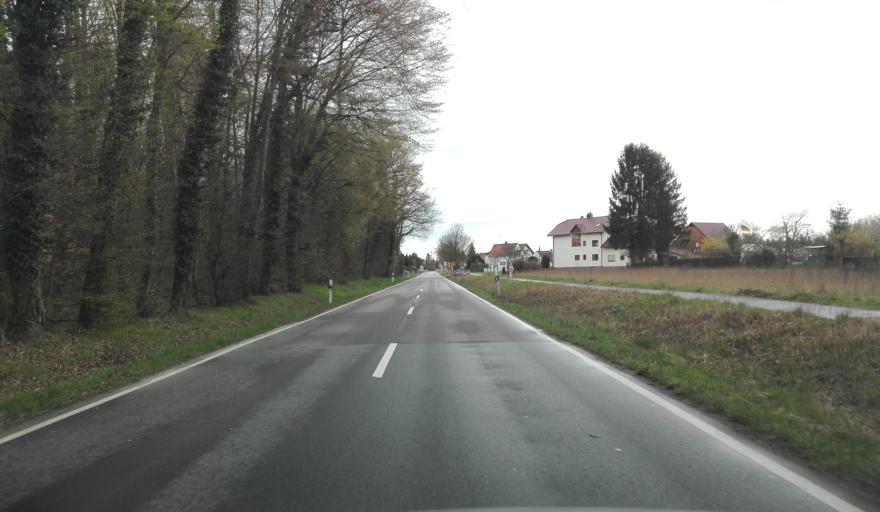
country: DE
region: Hesse
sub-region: Regierungsbezirk Darmstadt
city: Alsbach-Hahnlein
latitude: 49.7119
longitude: 8.5751
